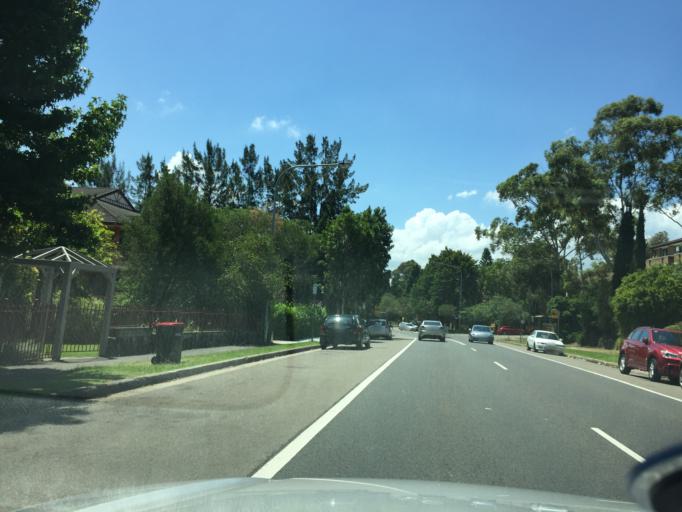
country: AU
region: New South Wales
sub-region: Parramatta
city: City of Parramatta
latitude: -33.8017
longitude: 151.0030
